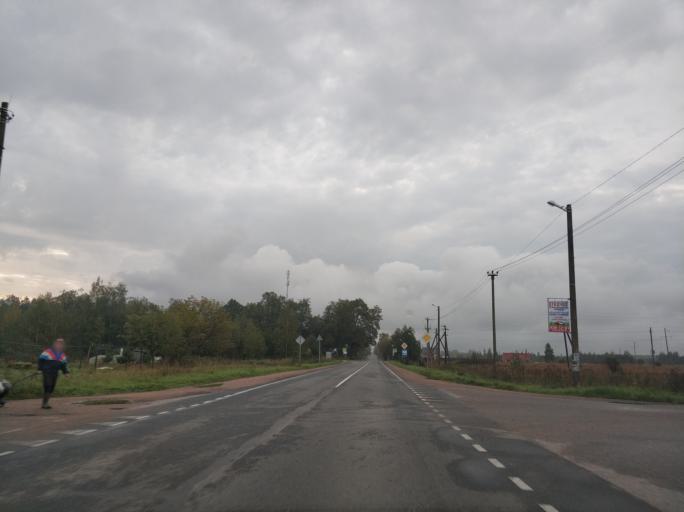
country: RU
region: Leningrad
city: Borisova Griva
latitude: 60.0841
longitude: 30.8940
